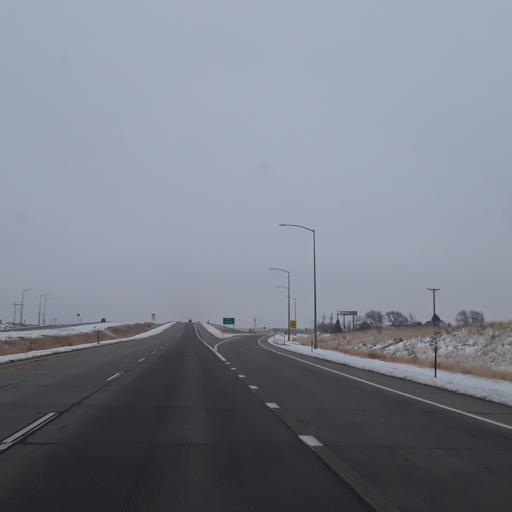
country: US
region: Colorado
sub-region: Logan County
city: Sterling
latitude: 40.4961
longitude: -103.2645
